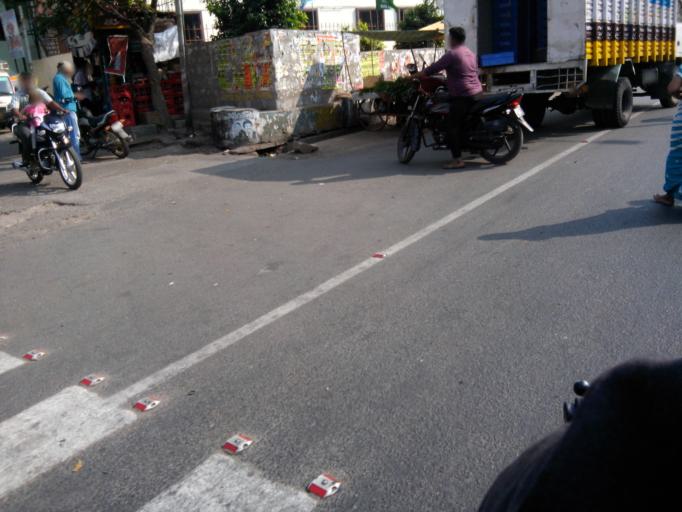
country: IN
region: Andhra Pradesh
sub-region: Krishna
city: Vijayawada
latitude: 16.5177
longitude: 80.6462
